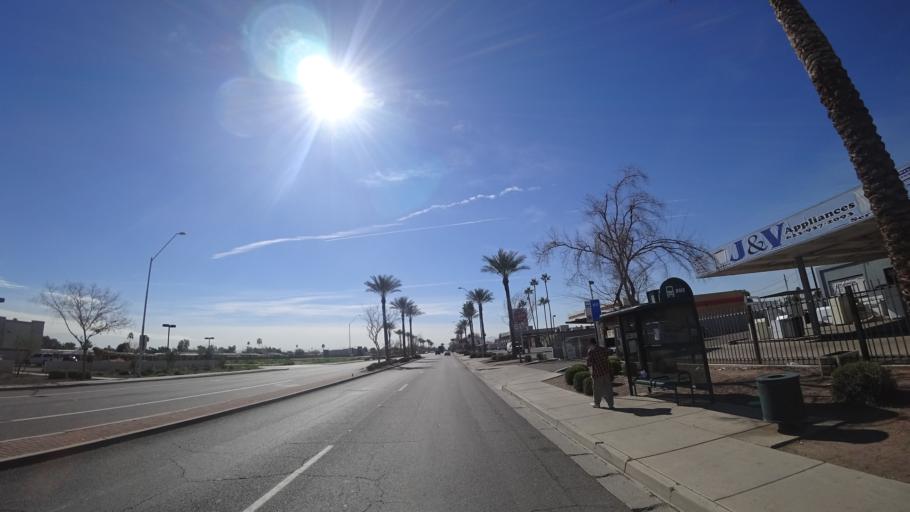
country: US
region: Arizona
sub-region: Maricopa County
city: Glendale
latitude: 33.5166
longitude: -112.1864
